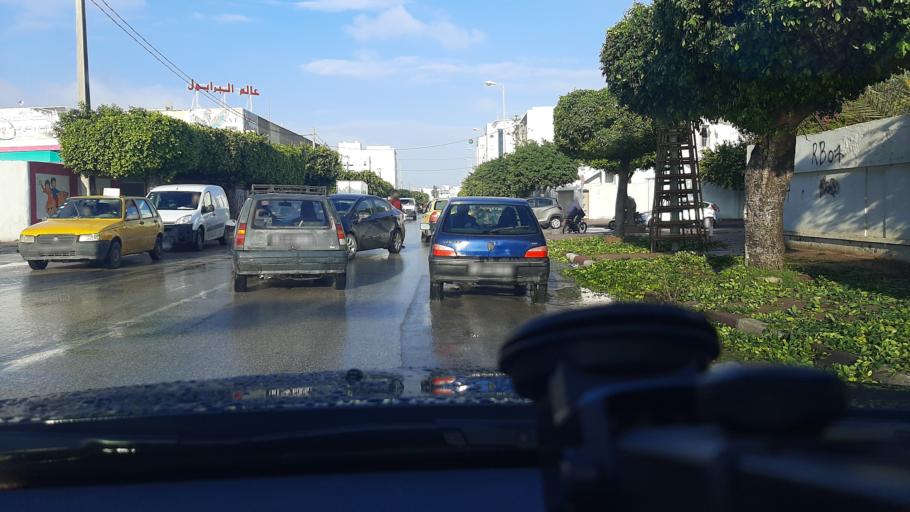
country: TN
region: Safaqis
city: Sfax
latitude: 34.7439
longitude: 10.7463
